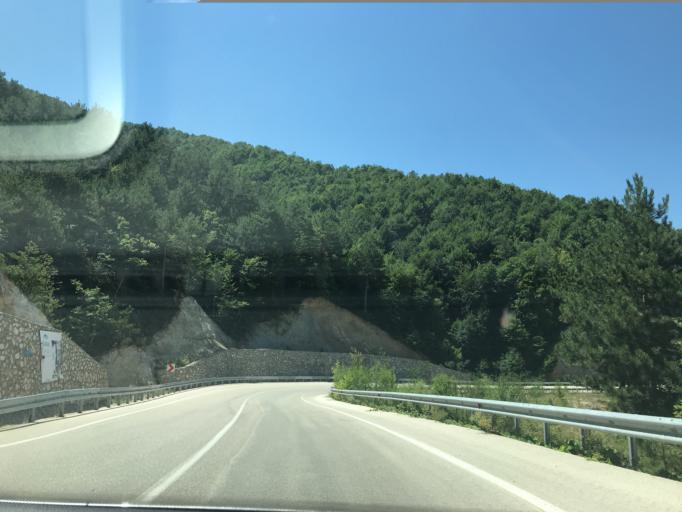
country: TR
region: Bursa
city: Tahtakopru
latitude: 39.9395
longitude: 29.5917
